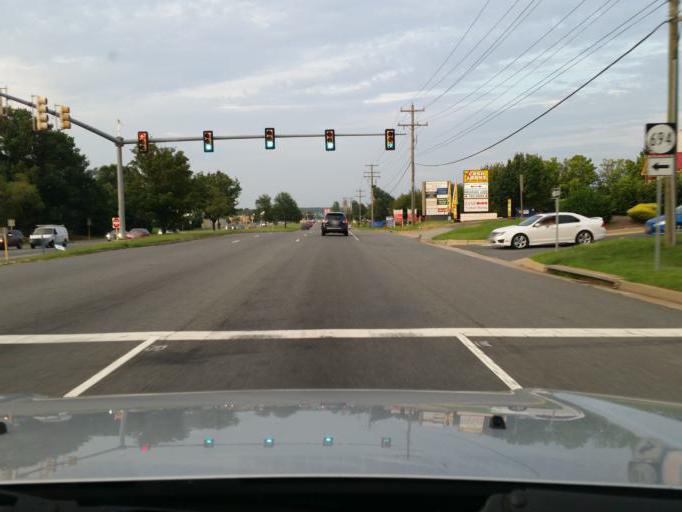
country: US
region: Virginia
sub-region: Stafford County
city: Falmouth
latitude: 38.2908
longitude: -77.5272
